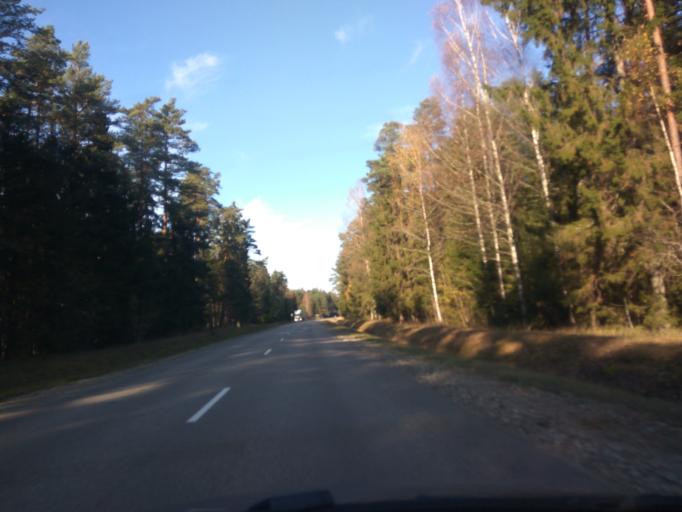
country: LV
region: Ventspils Rajons
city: Piltene
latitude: 57.0854
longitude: 21.7807
